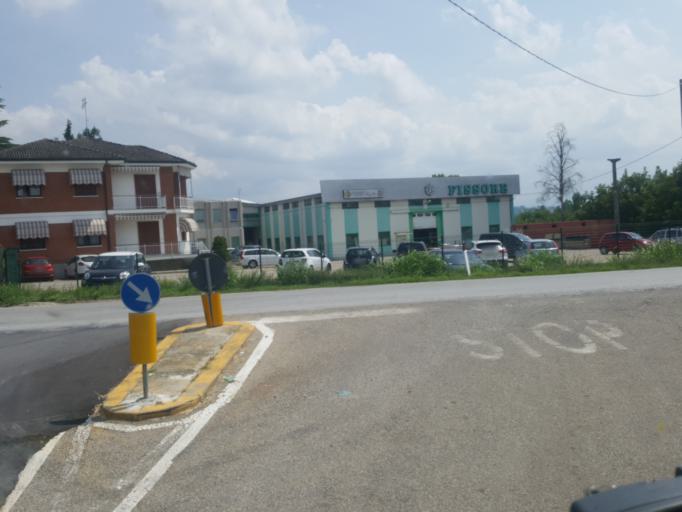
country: IT
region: Piedmont
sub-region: Provincia di Cuneo
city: Monchiero Borgonuovo
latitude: 44.5853
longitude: 7.9034
